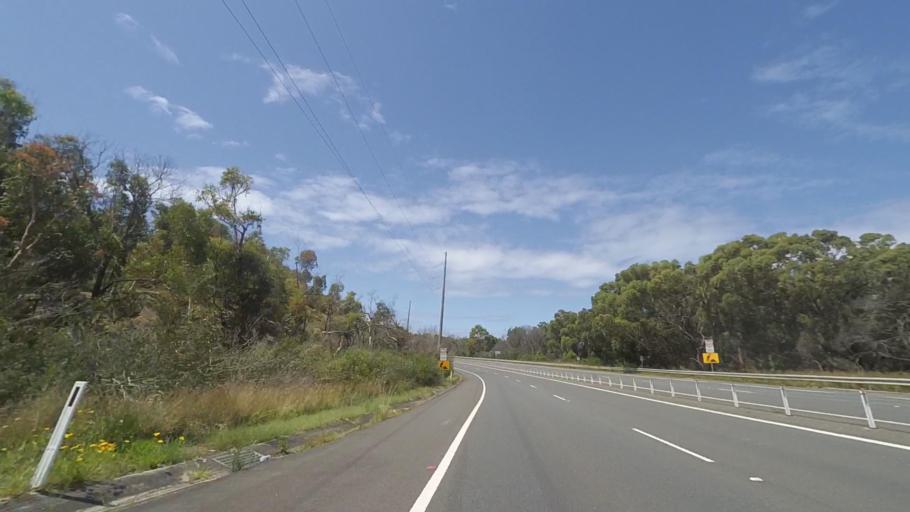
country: AU
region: New South Wales
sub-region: Wyong Shire
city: Kingfisher Shores
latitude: -33.1635
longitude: 151.6117
